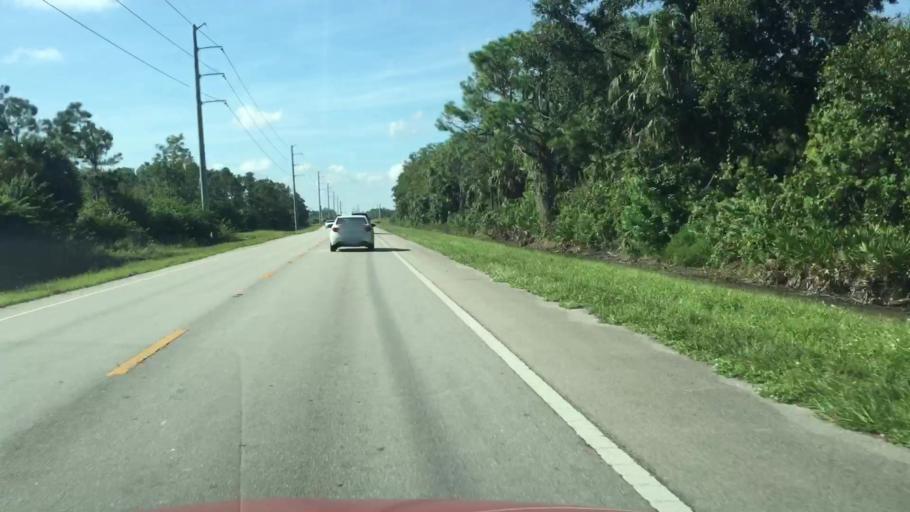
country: US
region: Florida
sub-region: Collier County
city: Orangetree
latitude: 26.3316
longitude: -81.5950
